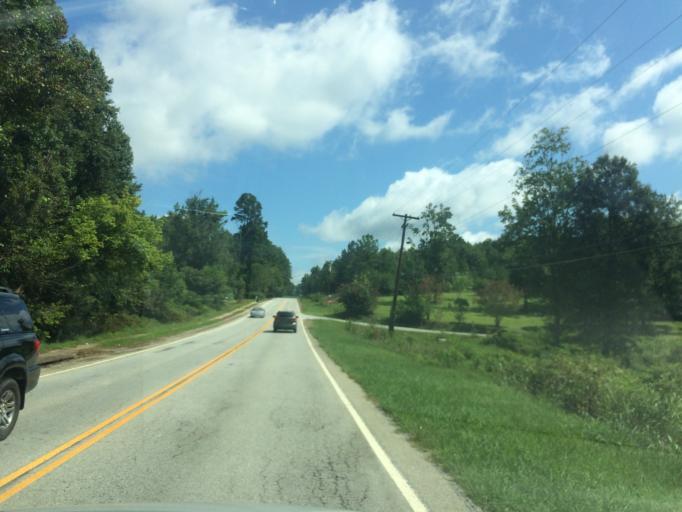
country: US
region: South Carolina
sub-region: Spartanburg County
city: Inman
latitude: 35.0551
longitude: -82.0850
